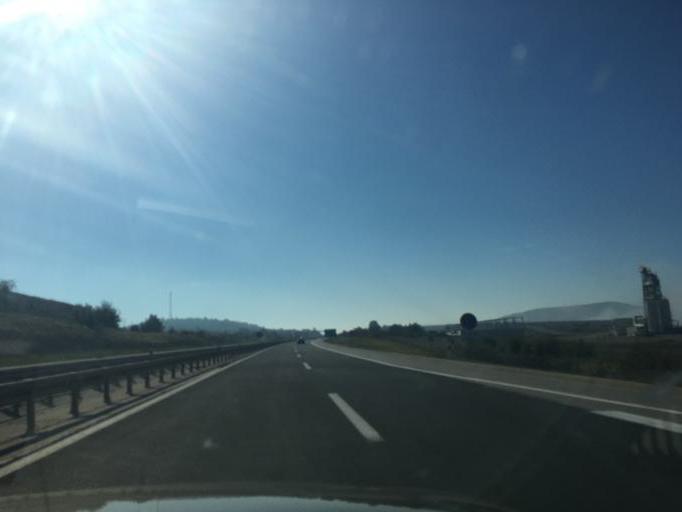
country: HR
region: Licko-Senjska
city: Gospic
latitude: 44.6670
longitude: 15.4218
